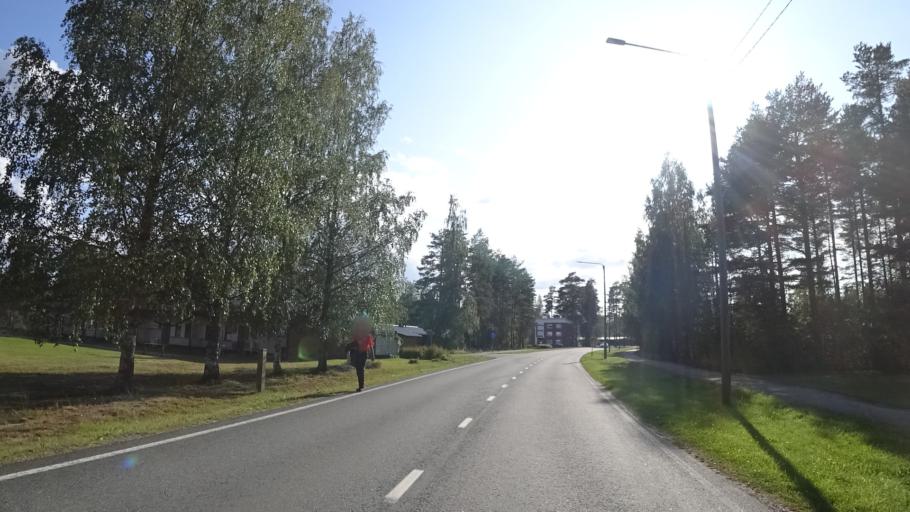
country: FI
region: North Karelia
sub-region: Keski-Karjala
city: Kesaelahti
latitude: 61.8919
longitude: 29.8414
